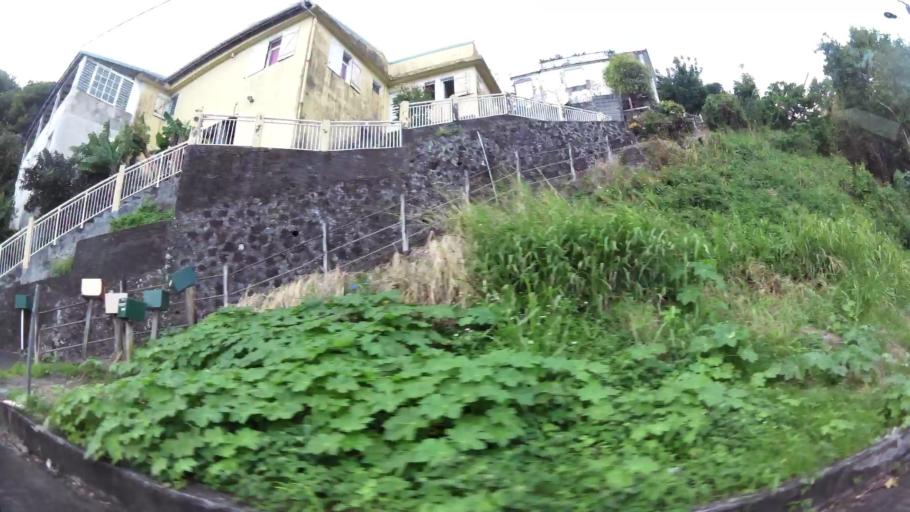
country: GP
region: Guadeloupe
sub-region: Guadeloupe
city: Trois-Rivieres
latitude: 15.9868
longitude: -61.6175
